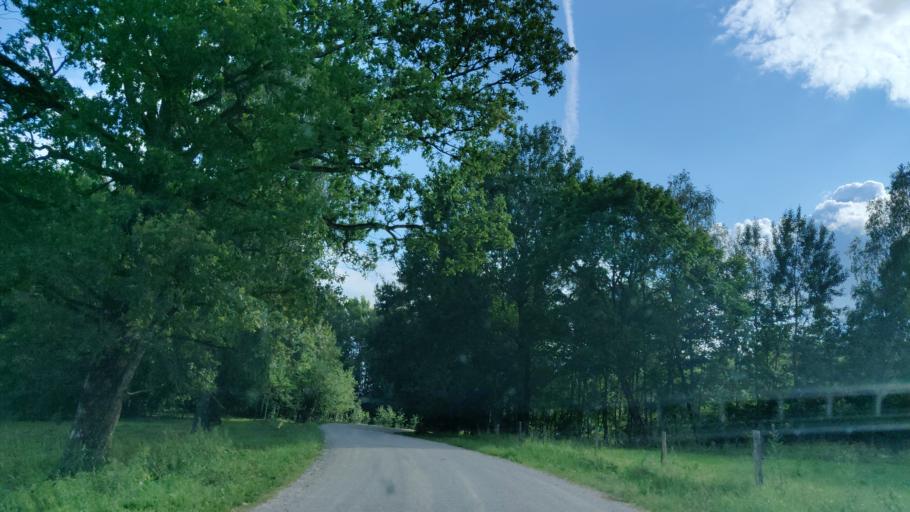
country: LT
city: Varniai
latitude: 55.6026
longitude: 22.3174
